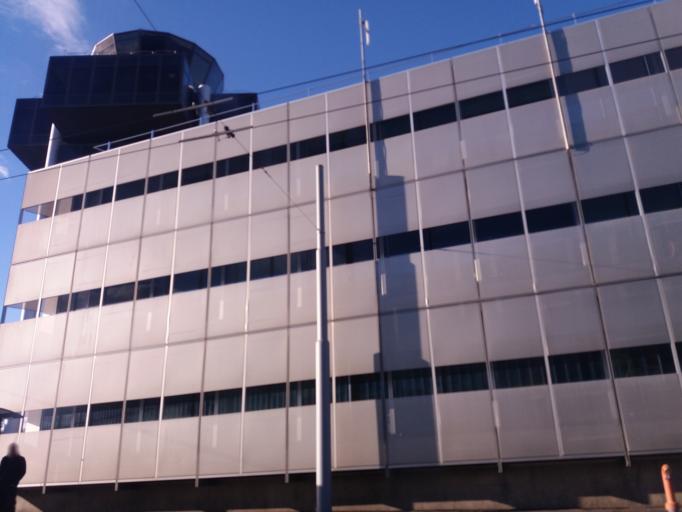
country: CH
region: Geneva
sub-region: Geneva
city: Les Avanchets
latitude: 46.2286
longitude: 6.1042
